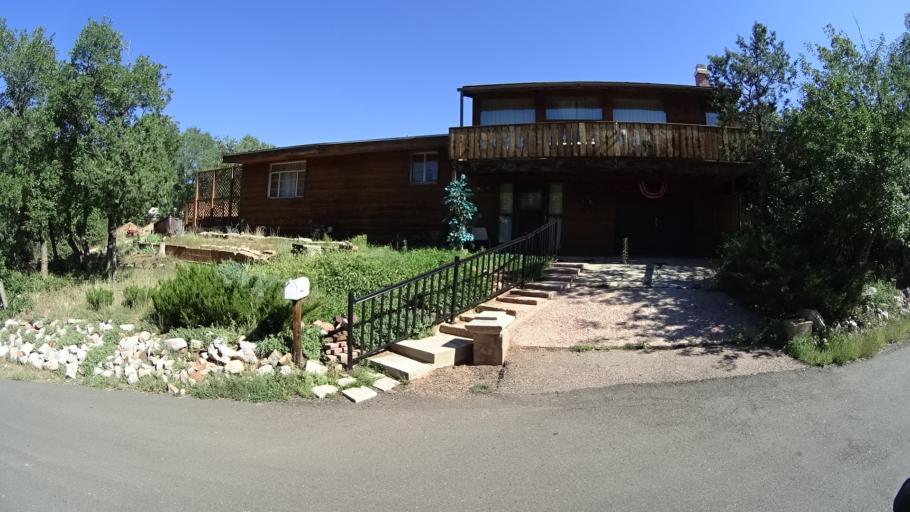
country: US
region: Colorado
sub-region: El Paso County
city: Manitou Springs
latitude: 38.8639
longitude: -104.8829
